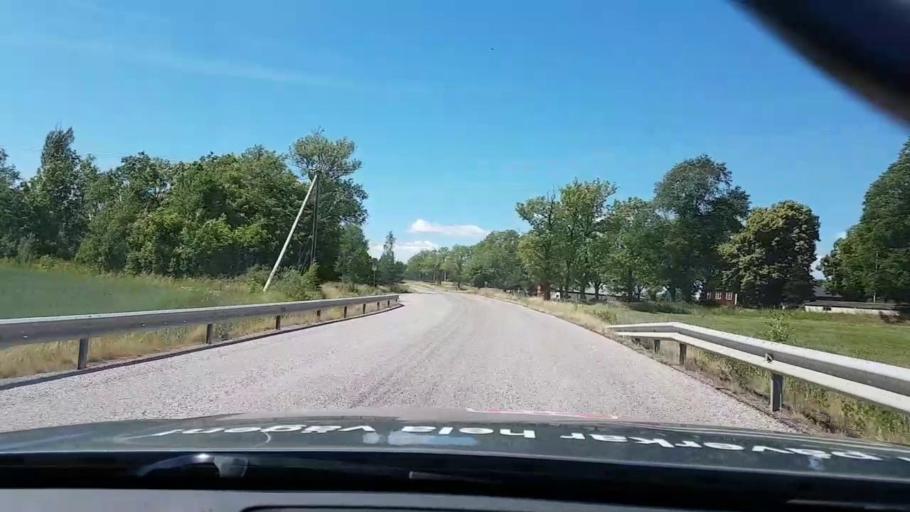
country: SE
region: Kalmar
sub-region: Vasterviks Kommun
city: Forserum
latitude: 57.9410
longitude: 16.4944
